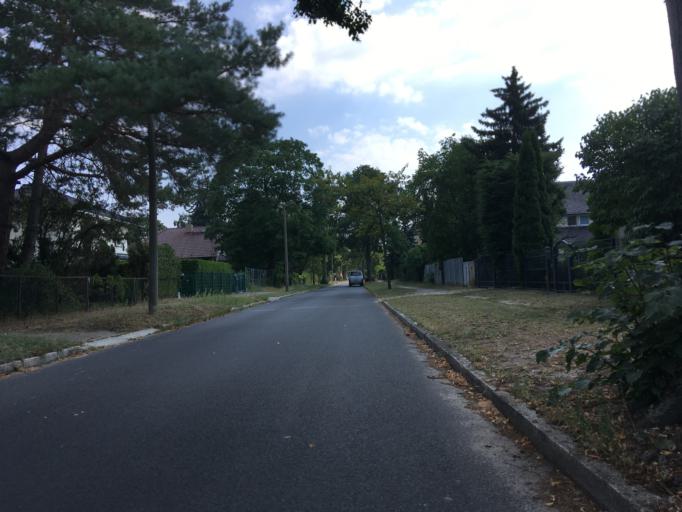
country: DE
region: Berlin
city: Mahlsdorf
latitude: 52.4892
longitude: 13.6094
